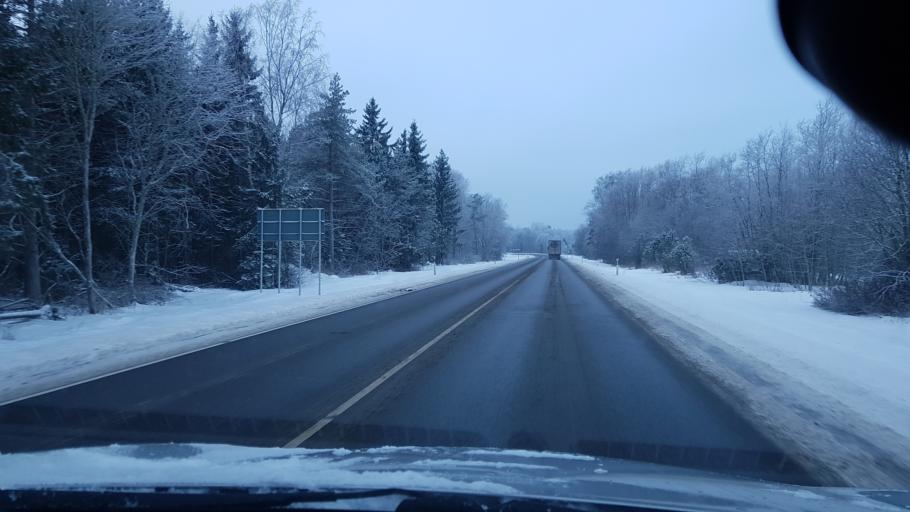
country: EE
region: Harju
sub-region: Paldiski linn
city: Paldiski
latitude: 59.3437
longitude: 24.1909
